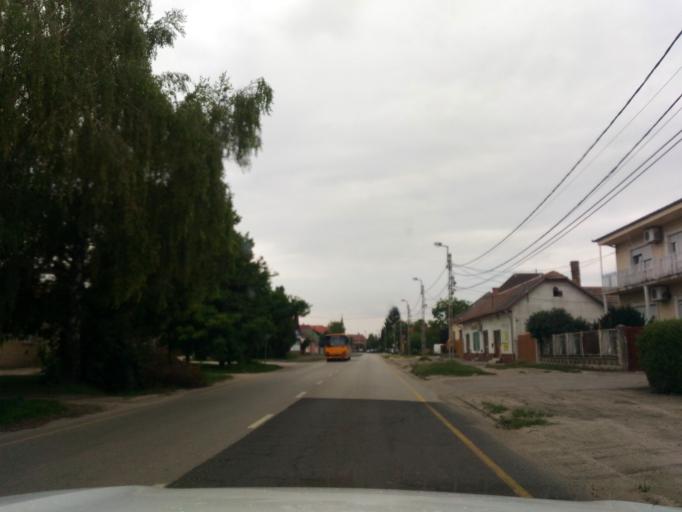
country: HU
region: Pest
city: Alsonemedi
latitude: 47.3096
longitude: 19.1731
